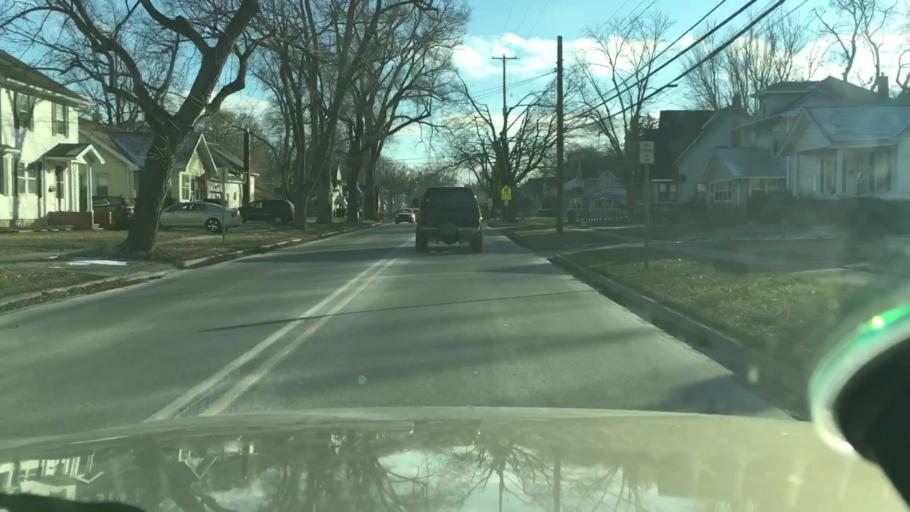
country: US
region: Michigan
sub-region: Jackson County
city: Jackson
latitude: 42.2382
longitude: -84.4234
